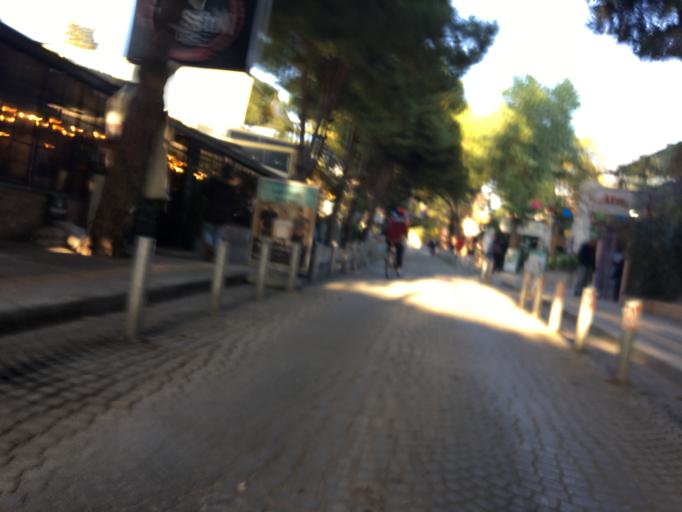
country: TR
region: Izmir
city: Buca
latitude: 38.3882
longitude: 27.1650
